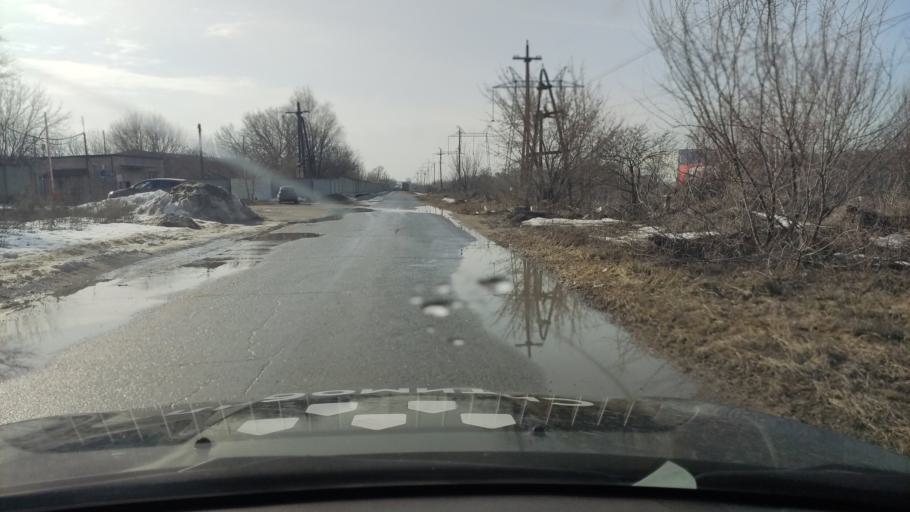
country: RU
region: Samara
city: Povolzhskiy
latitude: 53.5528
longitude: 49.6124
